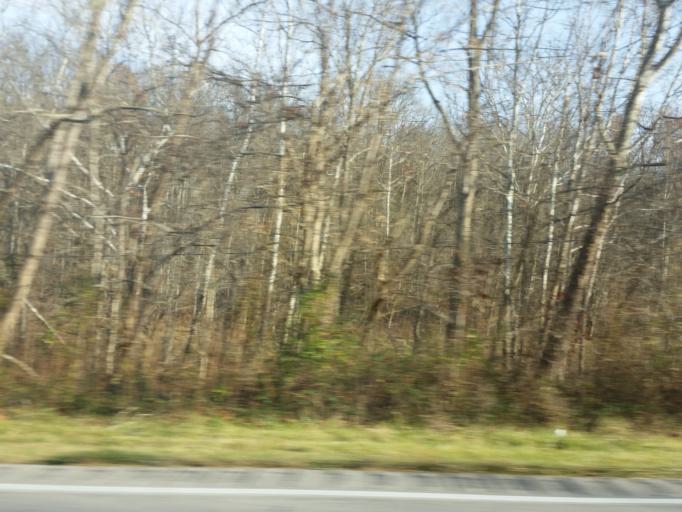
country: US
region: Kentucky
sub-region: Harrison County
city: Cynthiana
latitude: 38.5337
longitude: -84.2818
